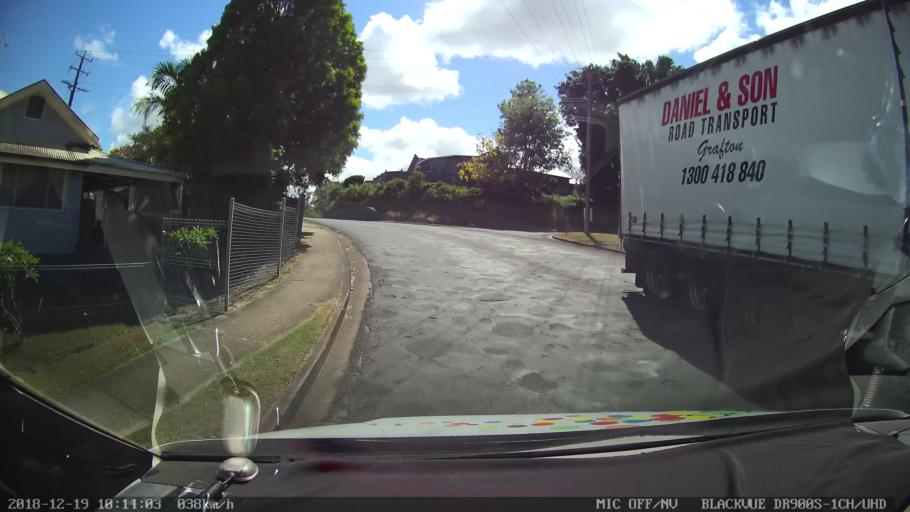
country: AU
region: New South Wales
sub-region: Kyogle
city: Kyogle
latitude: -28.6164
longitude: 153.0079
